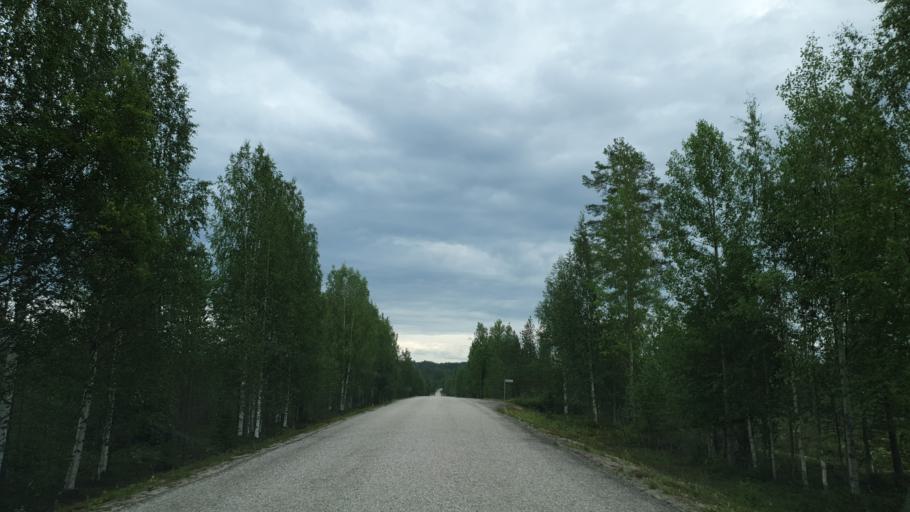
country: FI
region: Kainuu
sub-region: Kehys-Kainuu
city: Kuhmo
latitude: 64.3406
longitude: 29.3150
